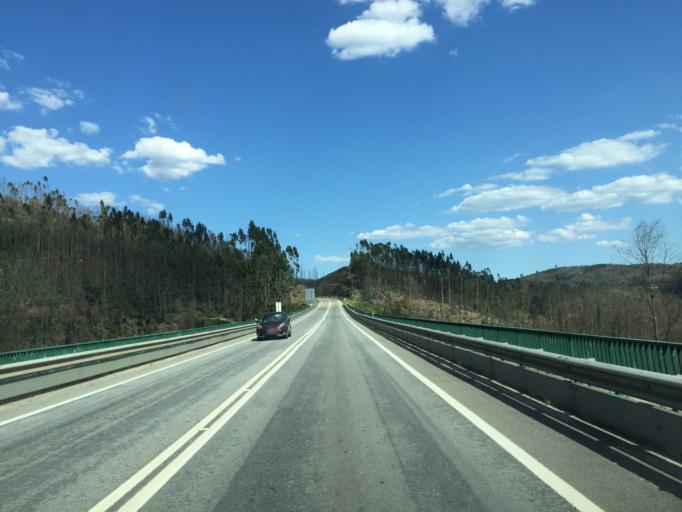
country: PT
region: Leiria
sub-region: Figueiro Dos Vinhos
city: Figueiro dos Vinhos
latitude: 39.9268
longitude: -8.3243
